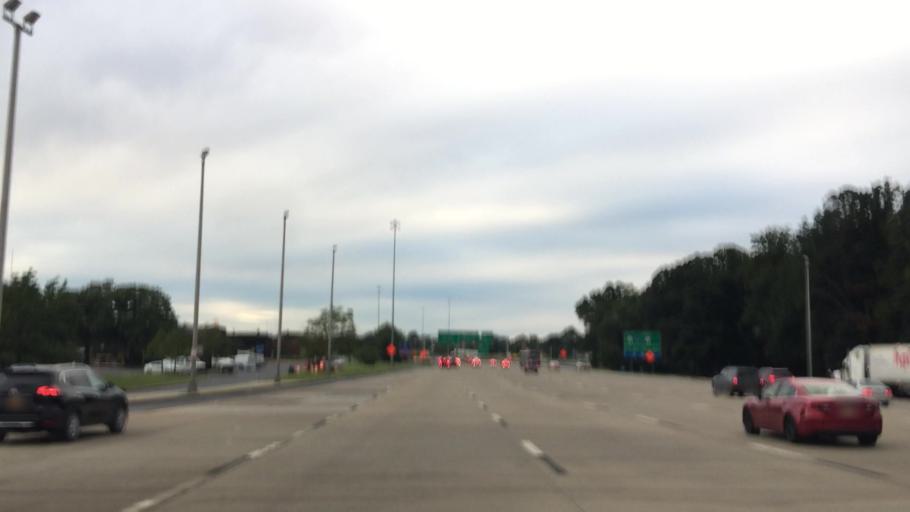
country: US
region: Delaware
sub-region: New Castle County
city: Wilmington Manor
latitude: 39.6963
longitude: -75.5465
